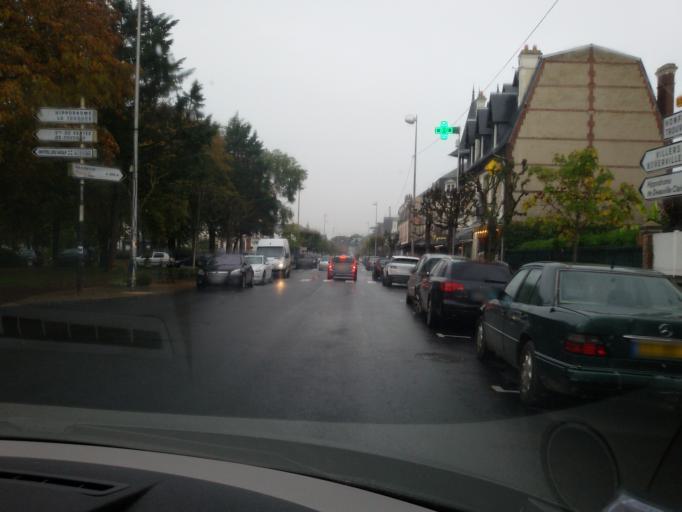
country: FR
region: Lower Normandy
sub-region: Departement du Calvados
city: Deauville
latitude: 49.3561
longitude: 0.0705
